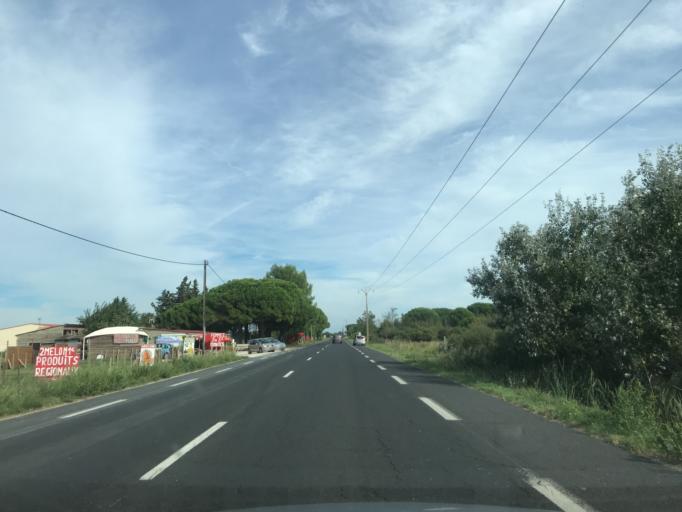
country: FR
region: Languedoc-Roussillon
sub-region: Departement du Gard
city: Aigues-Mortes
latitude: 43.5790
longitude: 4.2792
